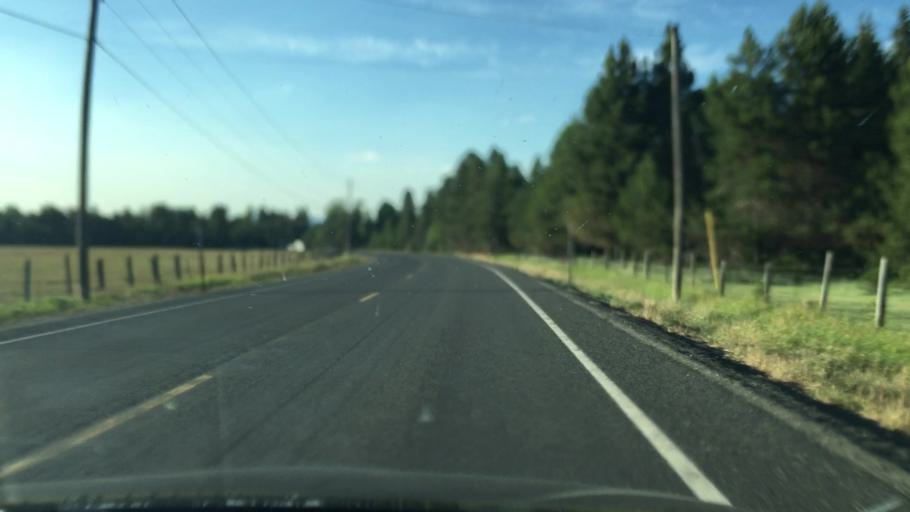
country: US
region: Idaho
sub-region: Valley County
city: McCall
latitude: 44.8217
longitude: -116.0781
